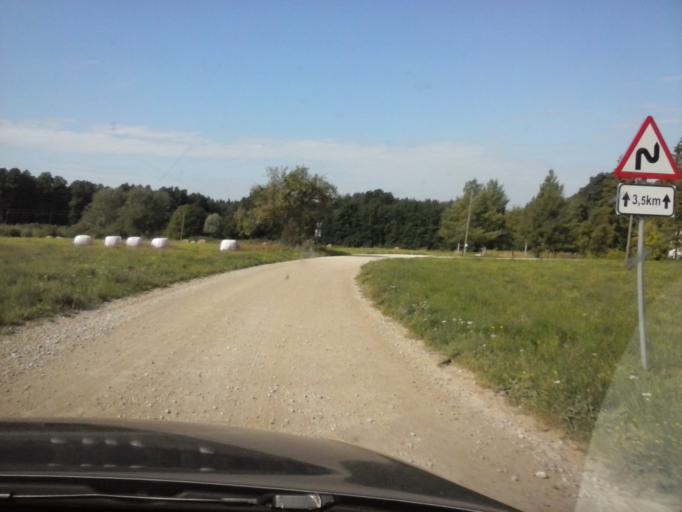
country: EE
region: Laeaene
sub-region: Ridala Parish
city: Uuemoisa
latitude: 58.8814
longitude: 23.6006
